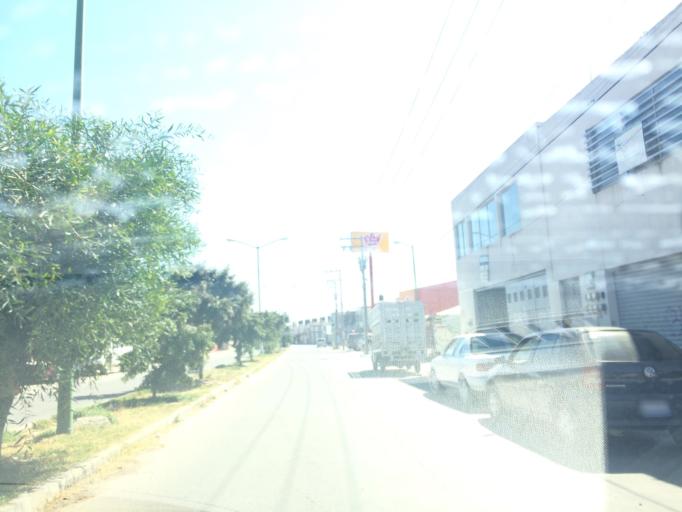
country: MX
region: Guanajuato
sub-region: Leon
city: San Jose de Duran (Los Troncoso)
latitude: 21.0928
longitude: -101.6687
